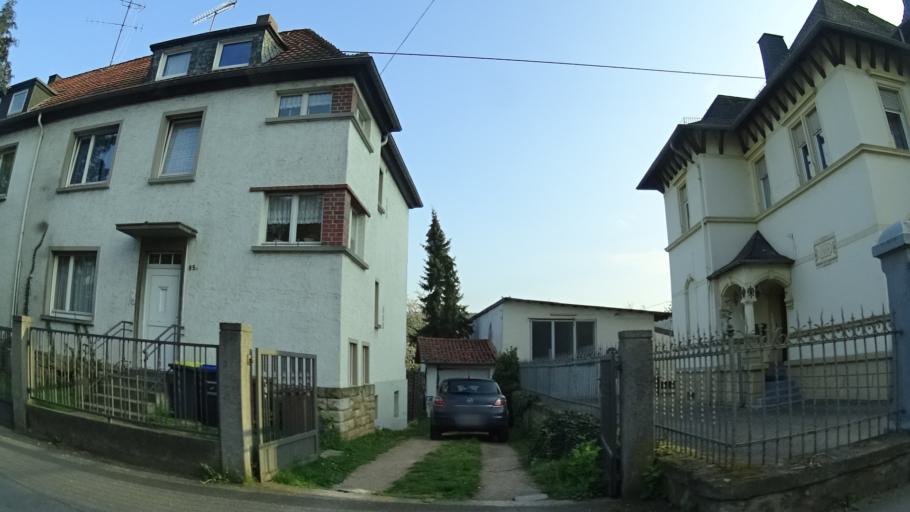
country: DE
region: Rheinland-Pfalz
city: Hargesheim
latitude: 49.8485
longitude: 7.8406
